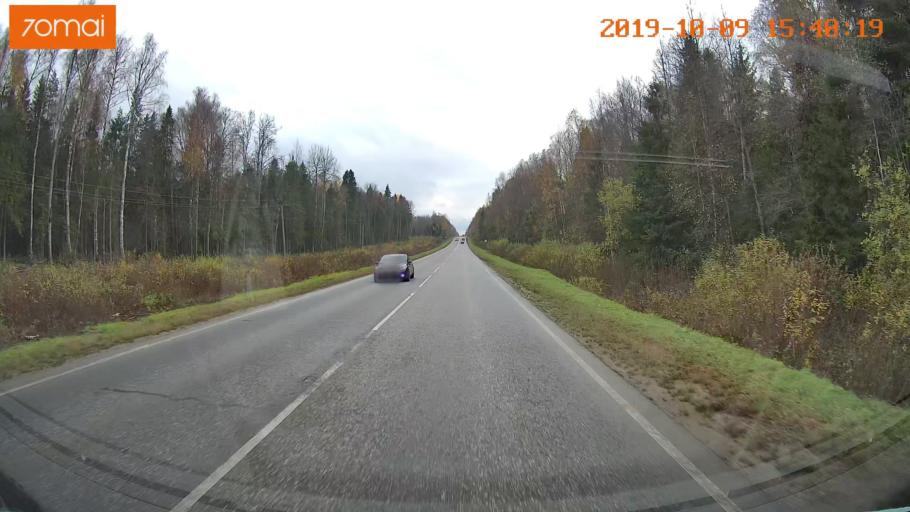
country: RU
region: Kostroma
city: Oktyabr'skiy
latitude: 57.8888
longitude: 41.1470
